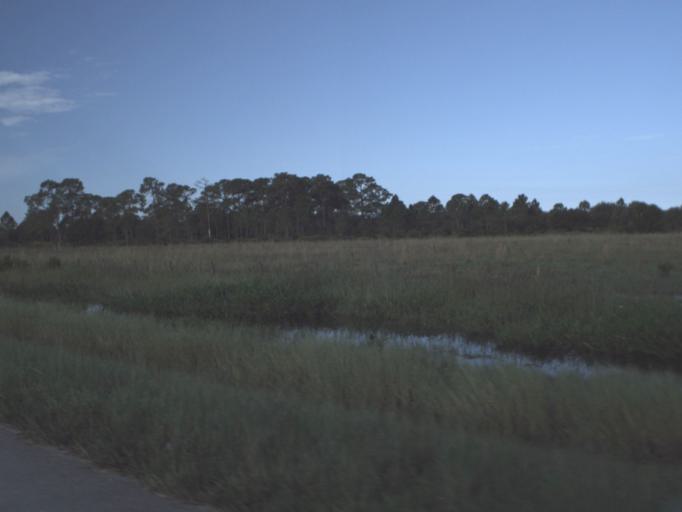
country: US
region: Florida
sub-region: Hendry County
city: Port LaBelle
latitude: 26.8468
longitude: -81.3832
